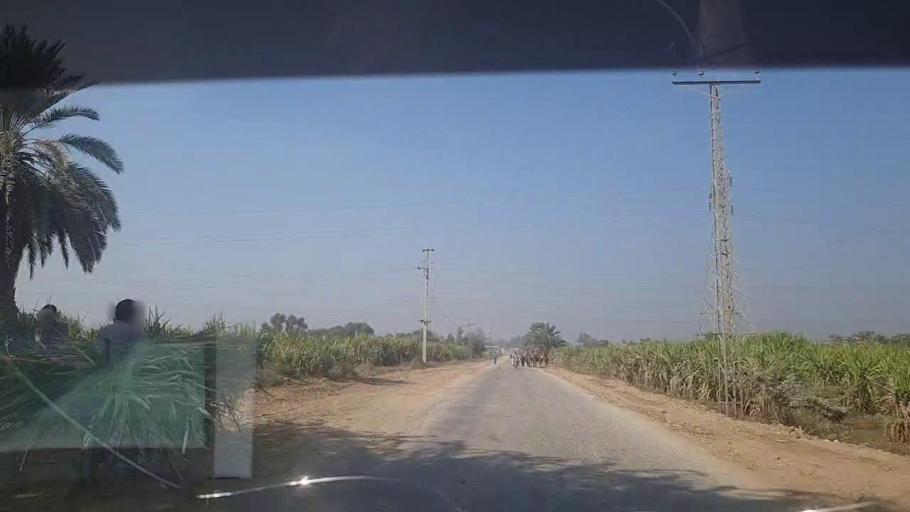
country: PK
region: Sindh
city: Kot Diji
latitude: 27.4269
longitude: 68.6557
